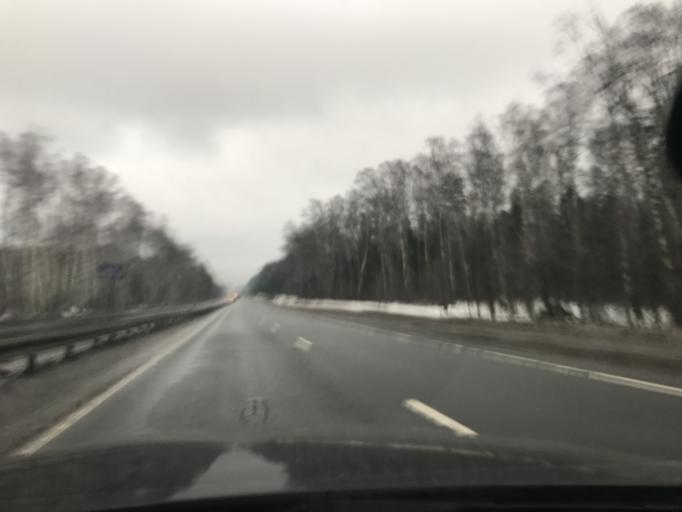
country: RU
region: Vladimir
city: Melekhovo
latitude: 56.2087
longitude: 41.2500
